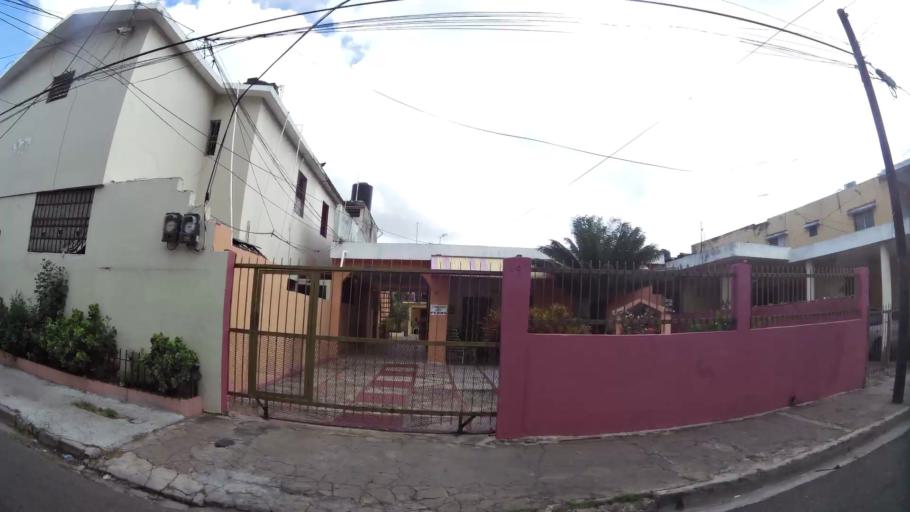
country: DO
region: Nacional
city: San Carlos
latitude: 18.4827
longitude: -69.9031
